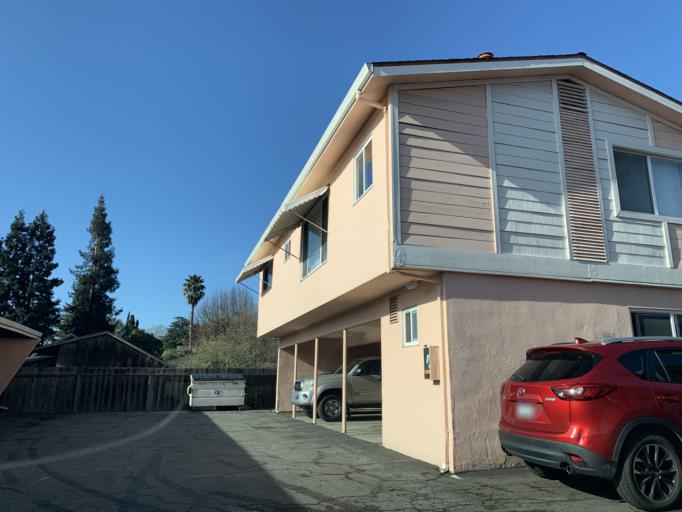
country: US
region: California
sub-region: Santa Clara County
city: Buena Vista
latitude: 37.3111
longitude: -121.9046
